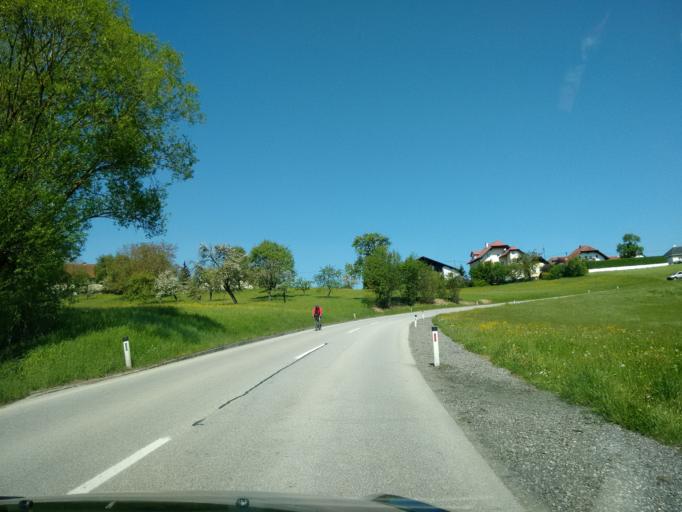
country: AT
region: Upper Austria
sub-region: Politischer Bezirk Steyr-Land
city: Waldneukirchen
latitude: 47.9932
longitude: 14.2589
